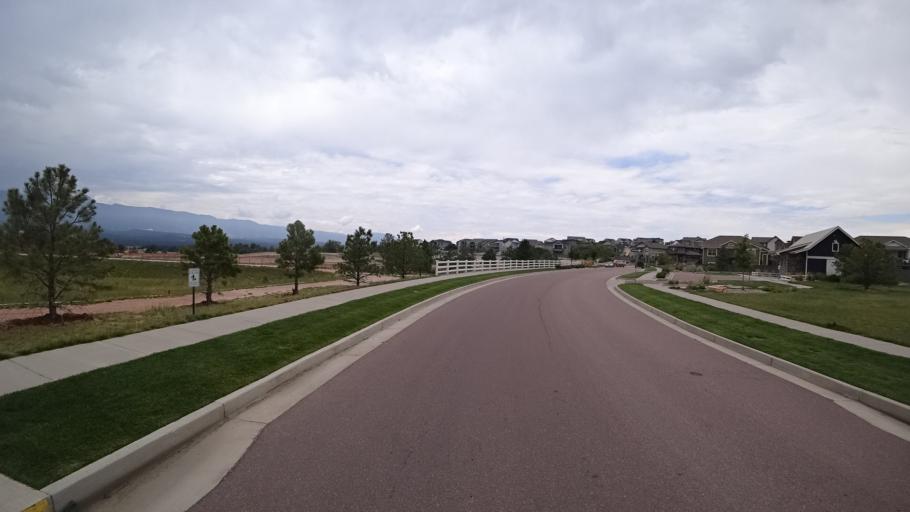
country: US
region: Colorado
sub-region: El Paso County
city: Gleneagle
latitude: 39.0005
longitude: -104.8052
